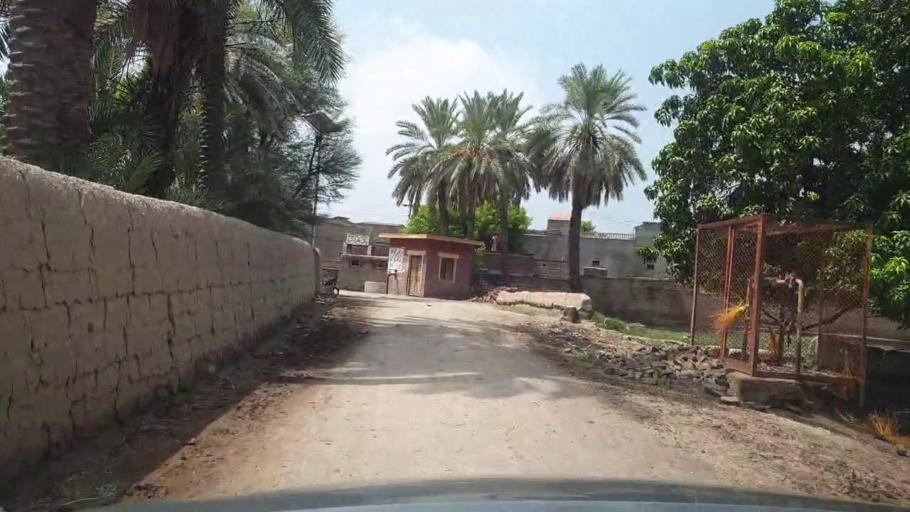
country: PK
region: Sindh
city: Pir jo Goth
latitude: 27.6127
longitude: 68.6747
